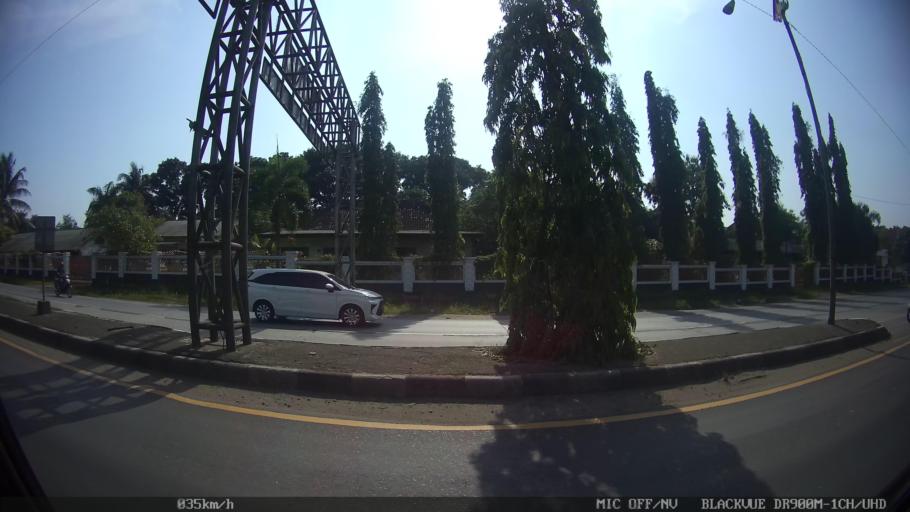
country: ID
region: Lampung
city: Natar
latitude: -5.2386
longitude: 105.1727
